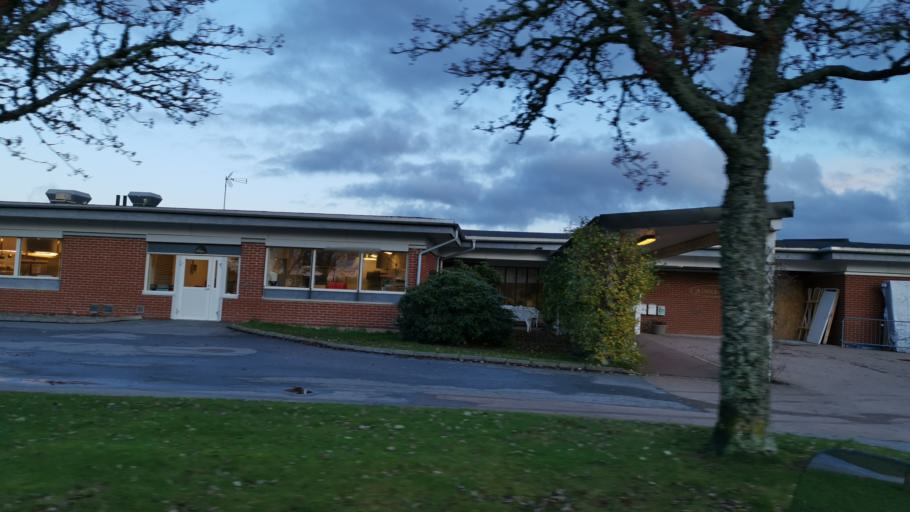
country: SE
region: Vaestra Goetaland
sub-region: Munkedals Kommun
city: Munkedal
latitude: 58.4743
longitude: 11.6708
